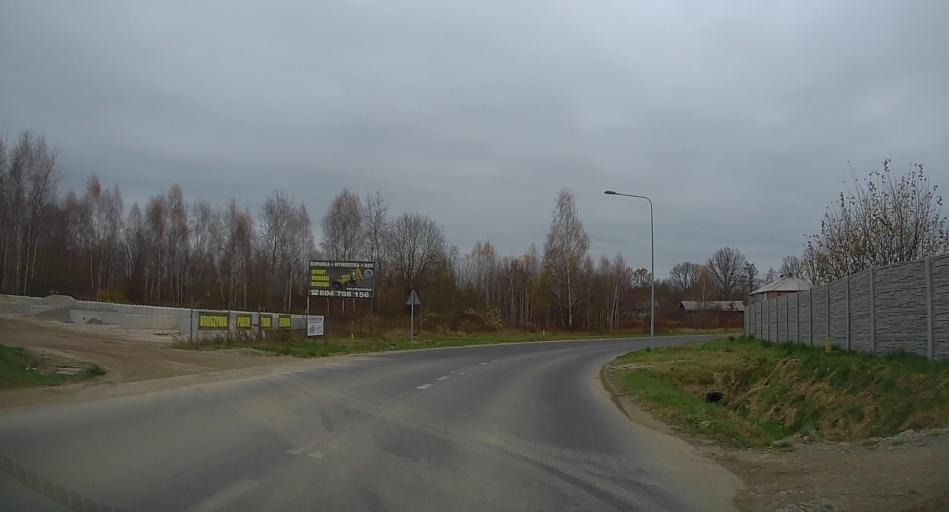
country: PL
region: Lodz Voivodeship
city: Zabia Wola
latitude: 52.0228
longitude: 20.6610
